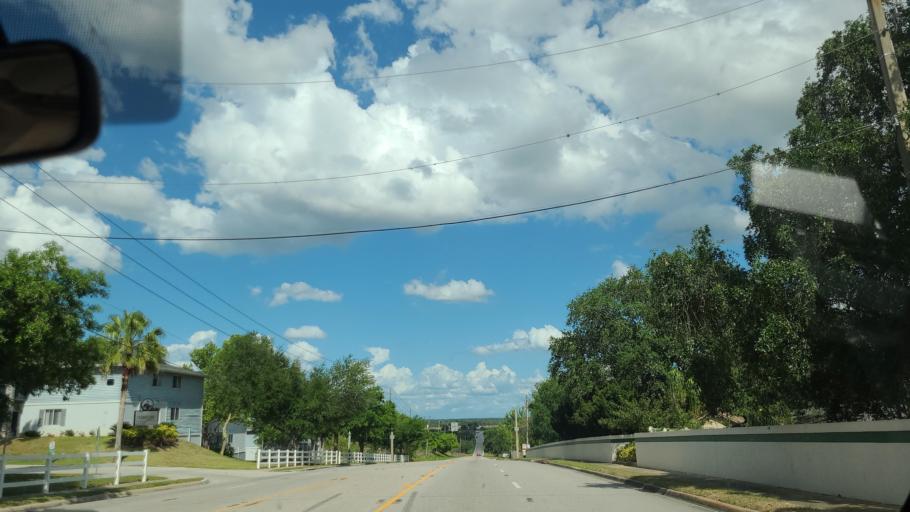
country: US
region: Florida
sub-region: Polk County
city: Lake Wales
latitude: 27.9139
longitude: -81.5635
